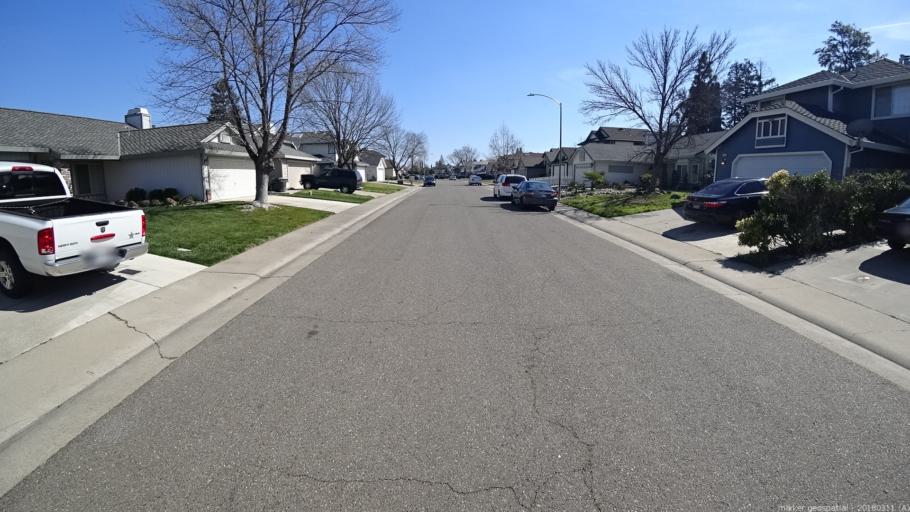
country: US
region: California
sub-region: Sacramento County
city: Florin
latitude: 38.4612
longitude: -121.3947
